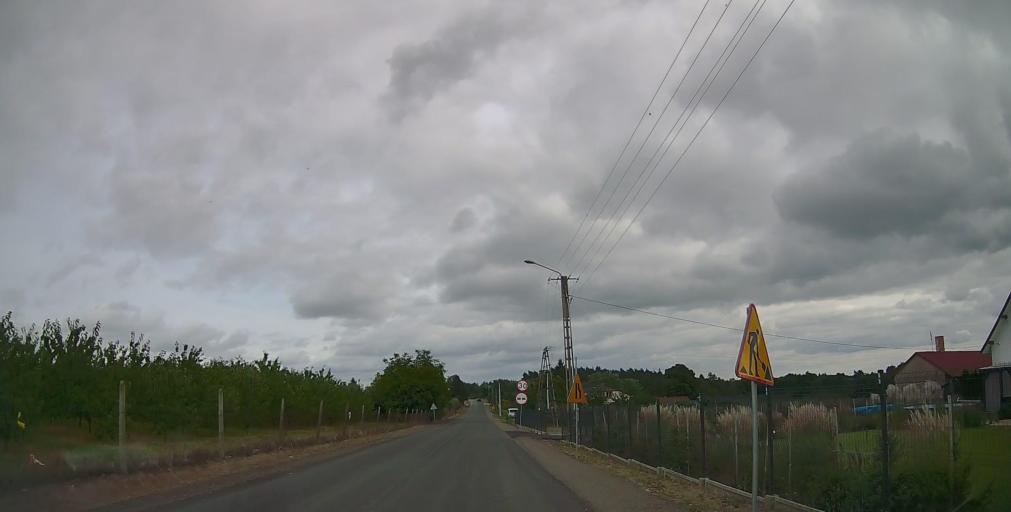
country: PL
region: Masovian Voivodeship
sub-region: Powiat grojecki
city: Belsk Duzy
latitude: 51.8091
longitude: 20.8428
